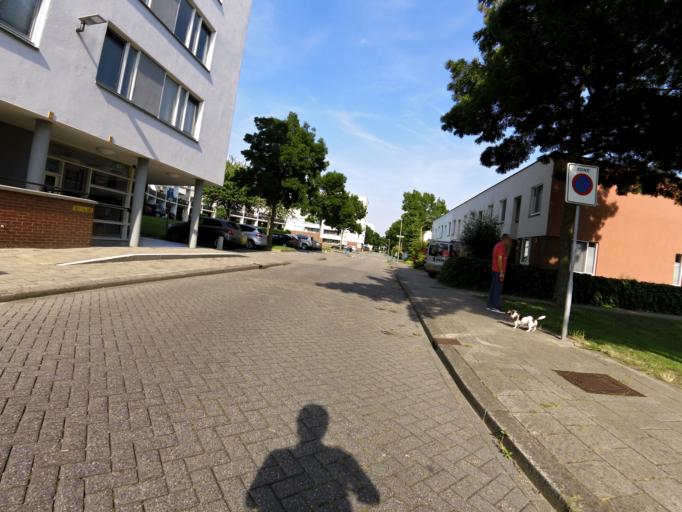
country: NL
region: South Holland
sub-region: Gemeente Papendrecht
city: Papendrecht
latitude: 51.8058
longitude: 4.7213
